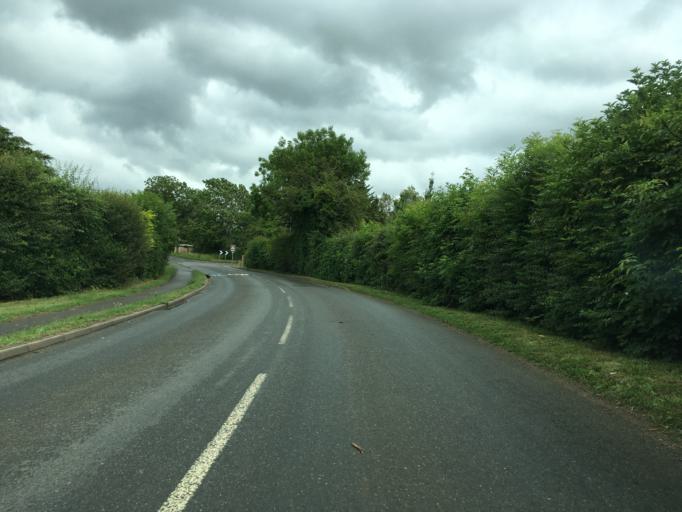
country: GB
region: England
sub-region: Worcestershire
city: Broadway
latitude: 52.0450
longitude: -1.8859
